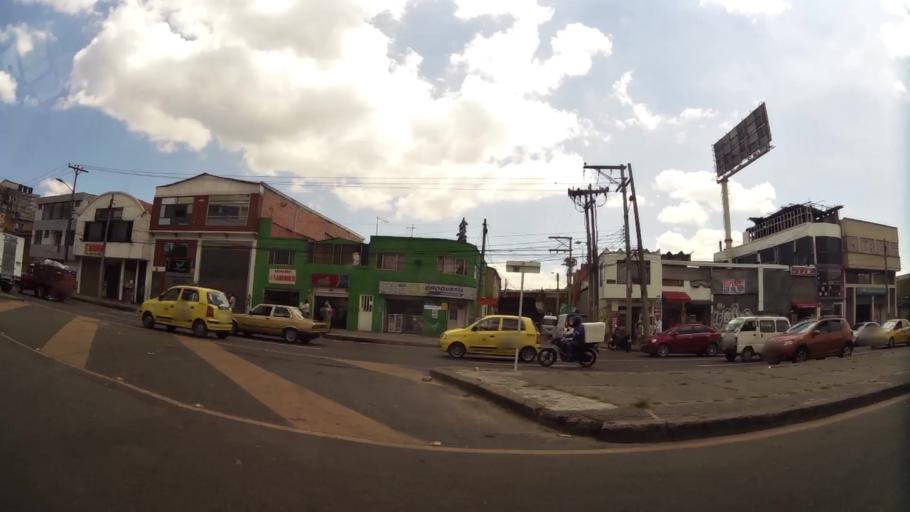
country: CO
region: Bogota D.C.
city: Bogota
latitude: 4.5809
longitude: -74.1018
